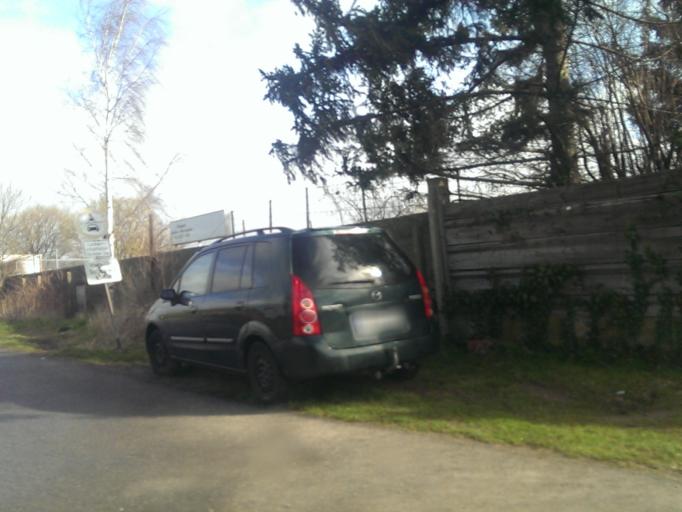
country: DE
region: Lower Saxony
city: Schellerten
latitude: 52.1689
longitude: 10.0545
